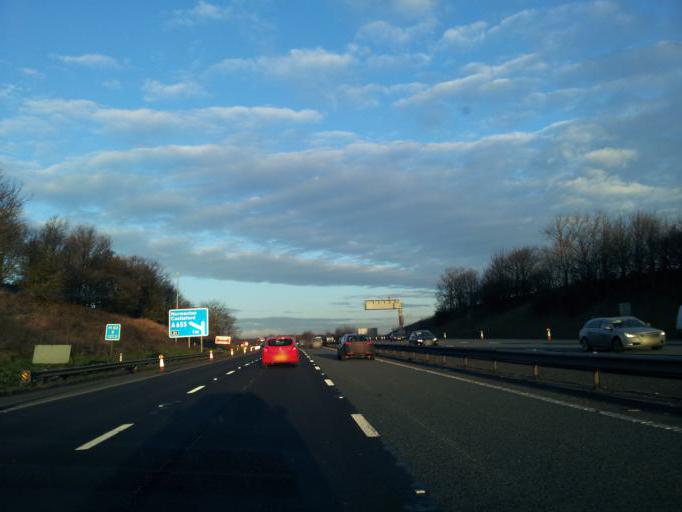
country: GB
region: England
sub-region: City and Borough of Wakefield
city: Castleford
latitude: 53.7059
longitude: -1.3633
